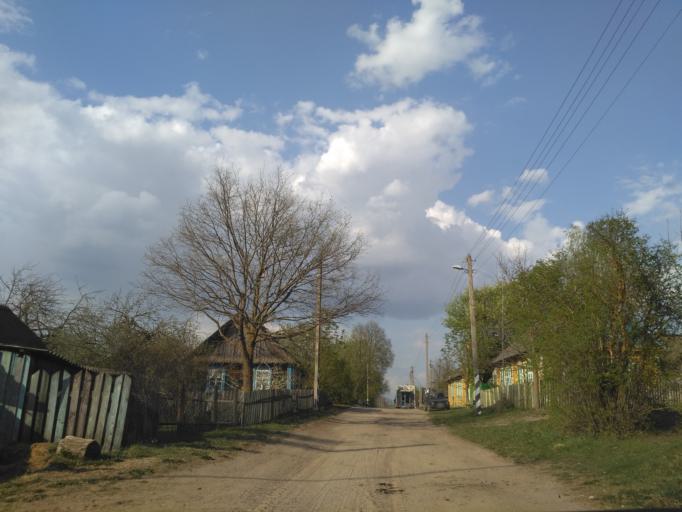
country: BY
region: Minsk
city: Khalopyenichy
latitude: 54.5015
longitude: 28.8465
